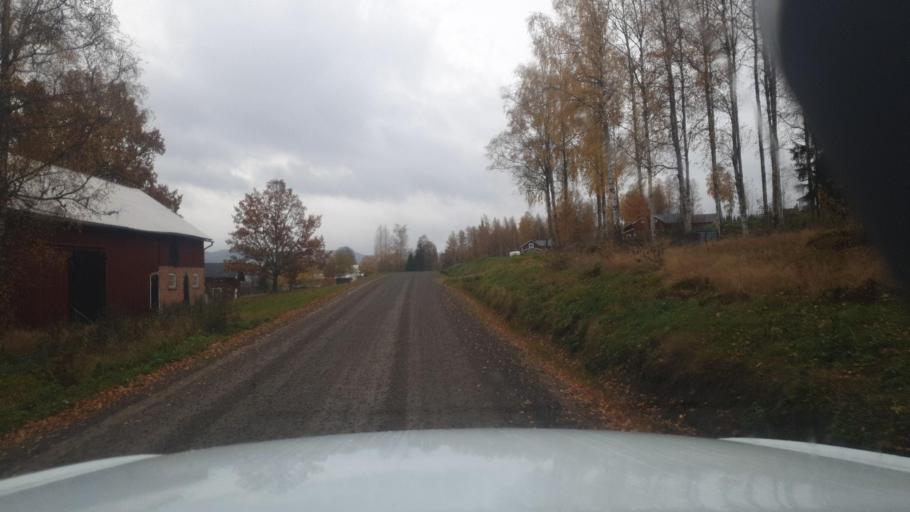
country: SE
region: Vaermland
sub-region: Torsby Kommun
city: Torsby
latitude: 59.9697
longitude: 12.8688
